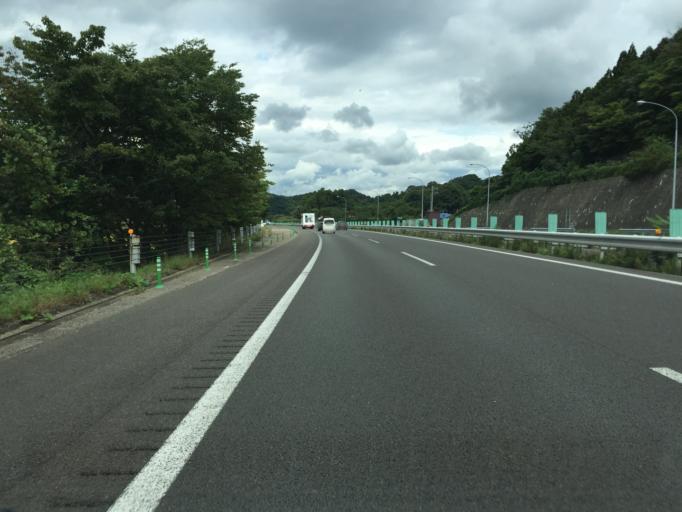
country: JP
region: Miyagi
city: Shiroishi
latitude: 37.9280
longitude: 140.6104
